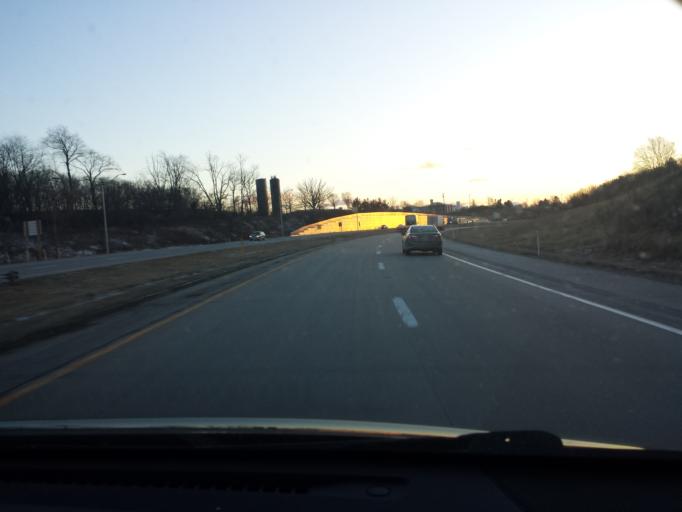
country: US
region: Pennsylvania
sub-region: Centre County
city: Pleasant Gap
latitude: 40.8884
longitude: -77.7342
